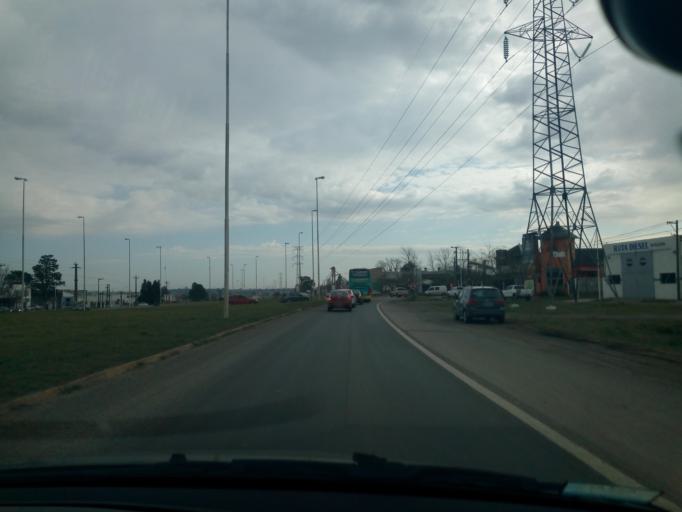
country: AR
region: Buenos Aires
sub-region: Partido de Tandil
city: Tandil
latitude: -37.3195
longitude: -59.1038
